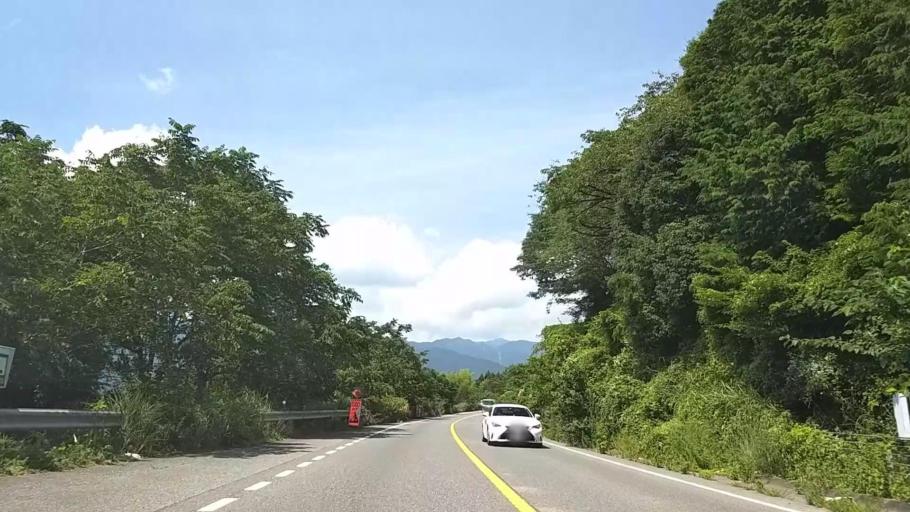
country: JP
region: Shizuoka
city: Fujinomiya
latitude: 35.3162
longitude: 138.5939
